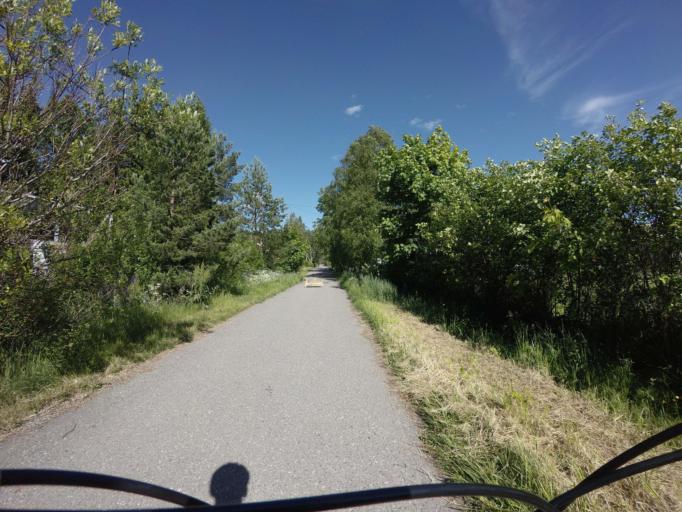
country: FI
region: Varsinais-Suomi
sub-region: Turku
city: Vahto
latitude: 60.5376
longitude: 22.3497
